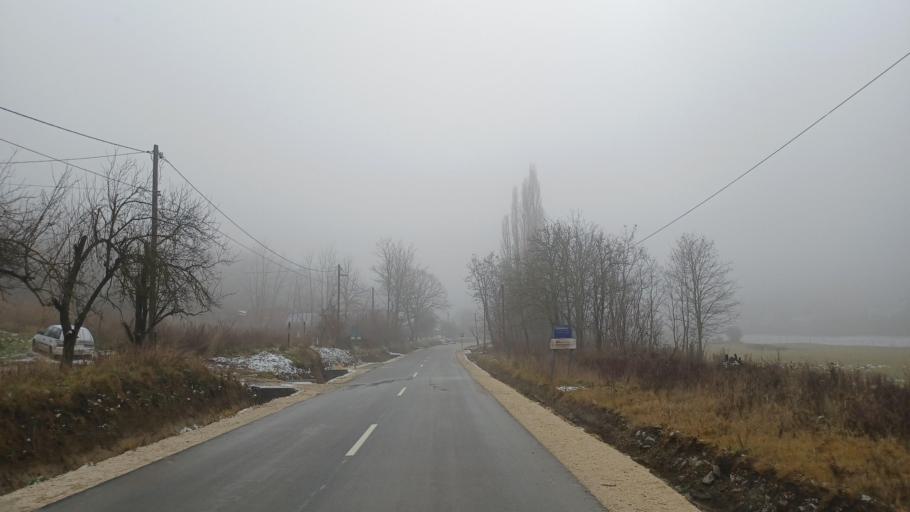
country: HU
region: Tolna
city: Gyonk
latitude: 46.5721
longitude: 18.4736
